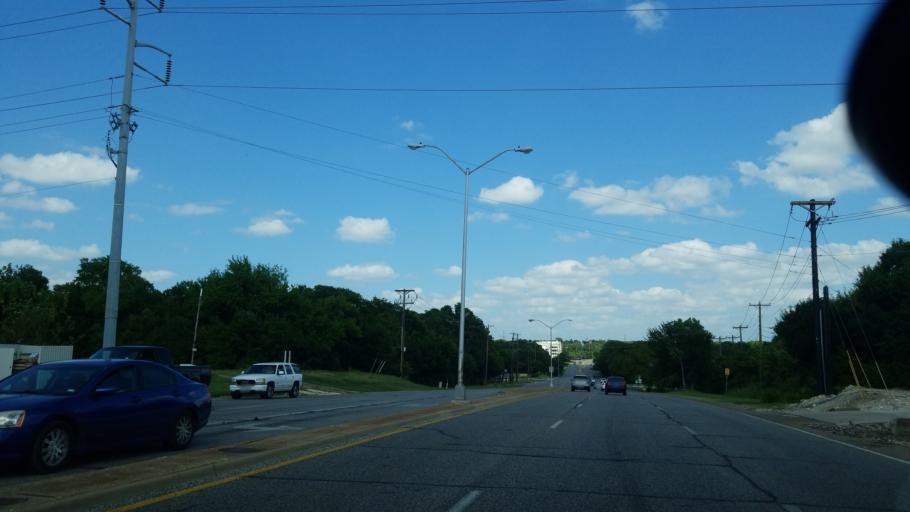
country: US
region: Texas
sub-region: Dallas County
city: Balch Springs
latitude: 32.7633
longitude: -96.7005
